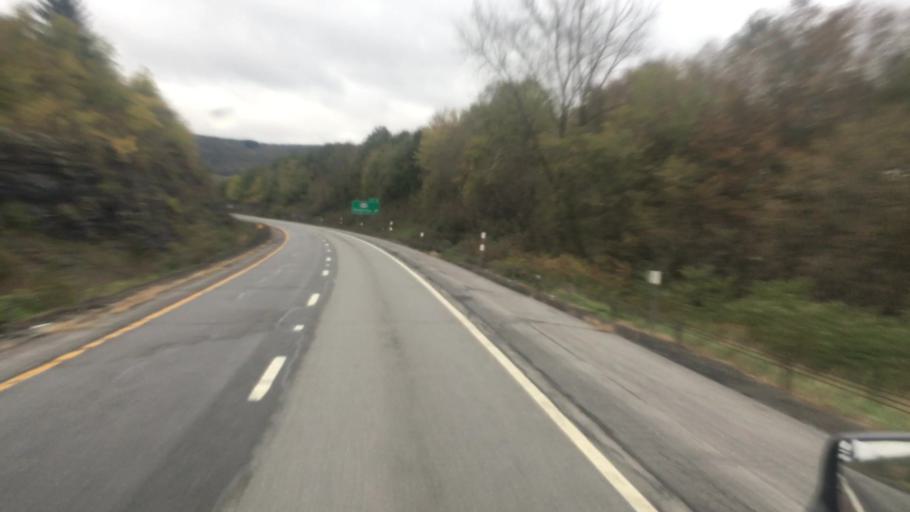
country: US
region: New York
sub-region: Chenango County
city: Bainbridge
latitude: 42.2946
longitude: -75.4632
